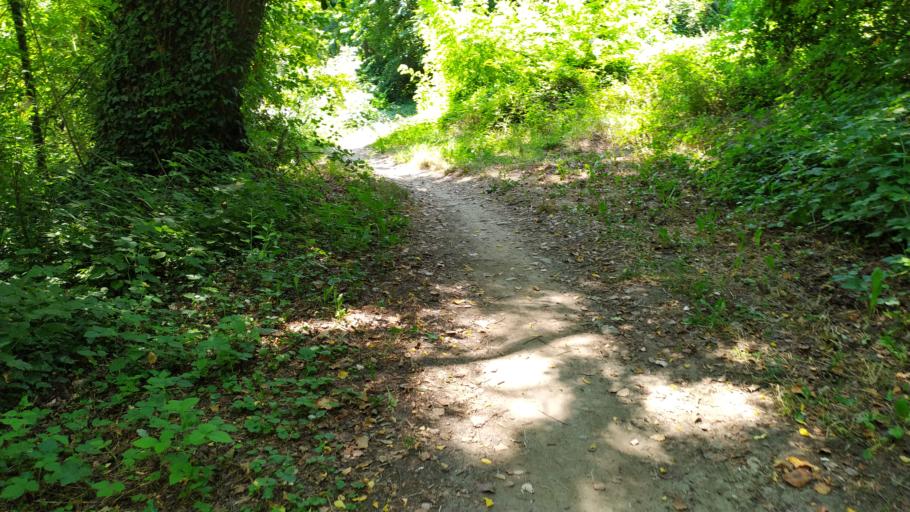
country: IT
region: Emilia-Romagna
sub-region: Forli-Cesena
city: Castrocaro Terme e Terra del Sole
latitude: 44.1920
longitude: 11.9754
